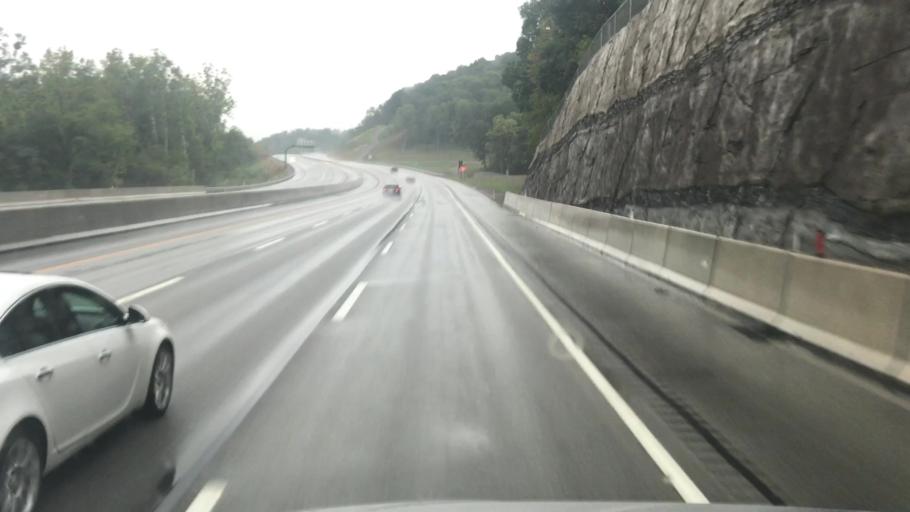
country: US
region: Pennsylvania
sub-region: Allegheny County
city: Oakmont
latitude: 40.5606
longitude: -79.8500
